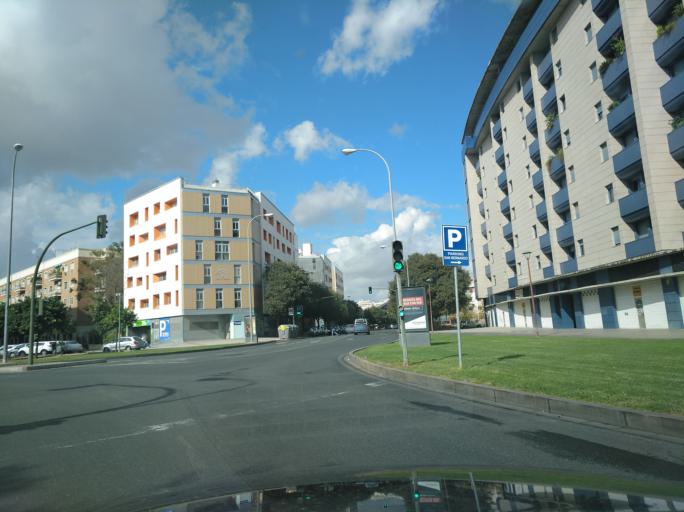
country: ES
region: Andalusia
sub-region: Provincia de Sevilla
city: Sevilla
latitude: 37.3799
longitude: -5.9828
